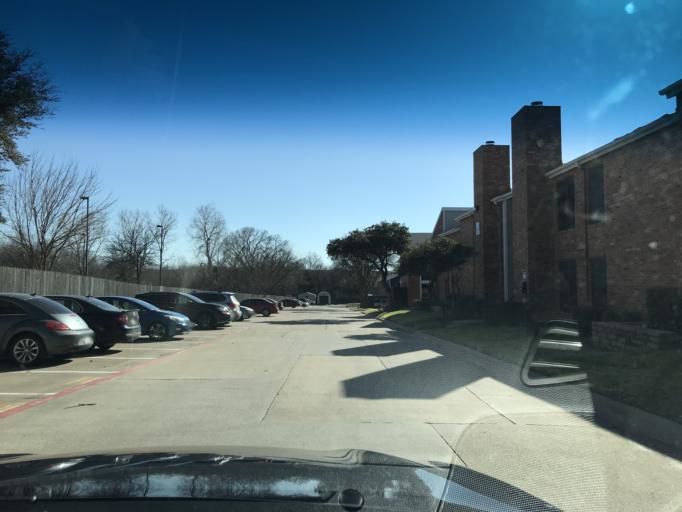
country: US
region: Texas
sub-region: Tarrant County
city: Benbrook
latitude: 32.6754
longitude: -97.4045
